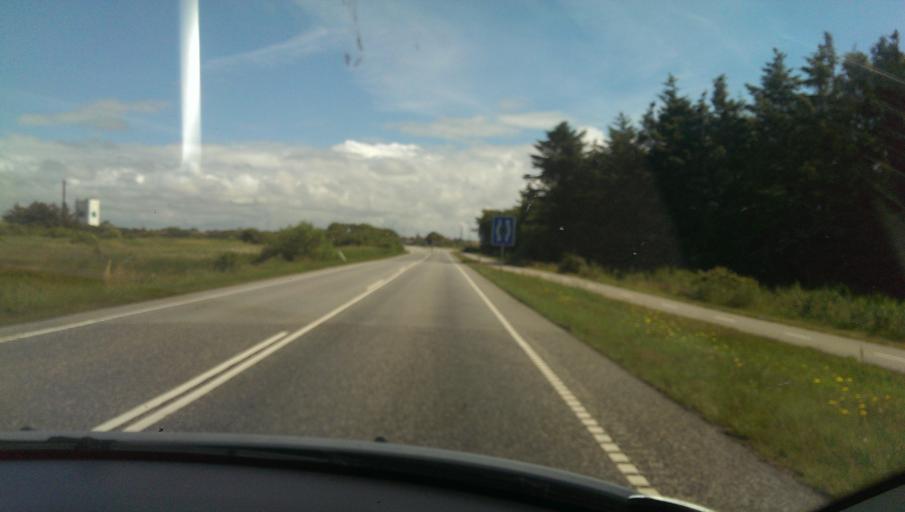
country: DK
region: Central Jutland
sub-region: Ringkobing-Skjern Kommune
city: Ringkobing
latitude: 56.0976
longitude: 8.2282
